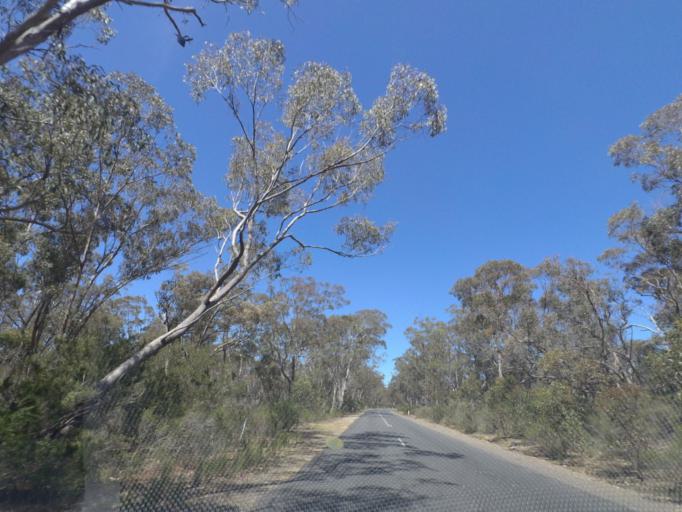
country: AU
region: Victoria
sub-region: Melton
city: Melton West
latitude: -37.6349
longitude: 144.5087
